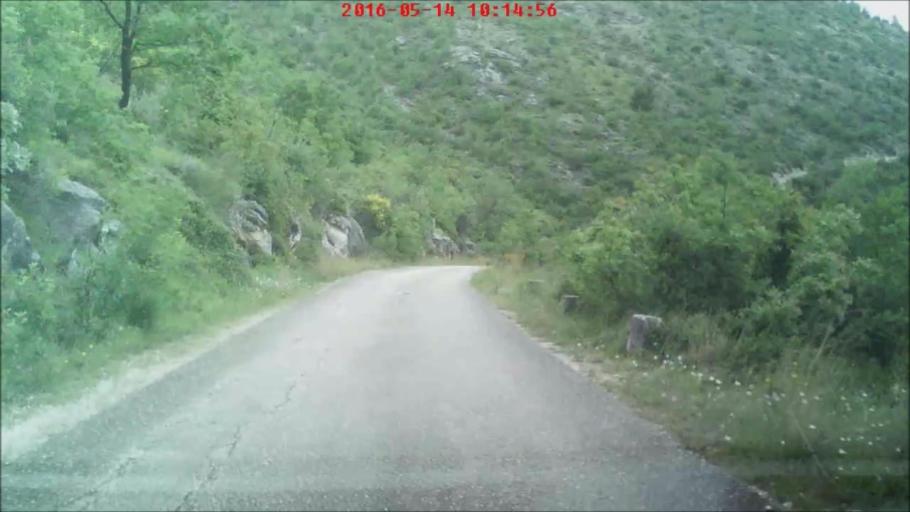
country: HR
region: Dubrovacko-Neretvanska
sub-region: Grad Dubrovnik
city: Mokosica
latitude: 42.7322
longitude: 17.9615
